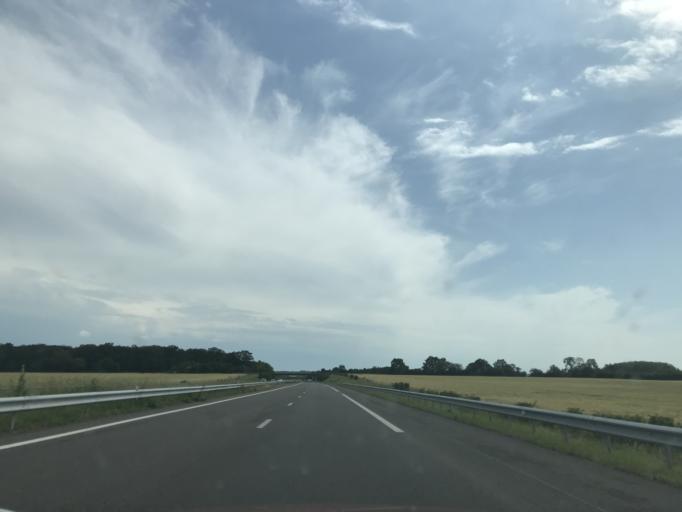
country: FR
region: Centre
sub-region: Departement du Cher
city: Orval
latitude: 46.8072
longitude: 2.4125
